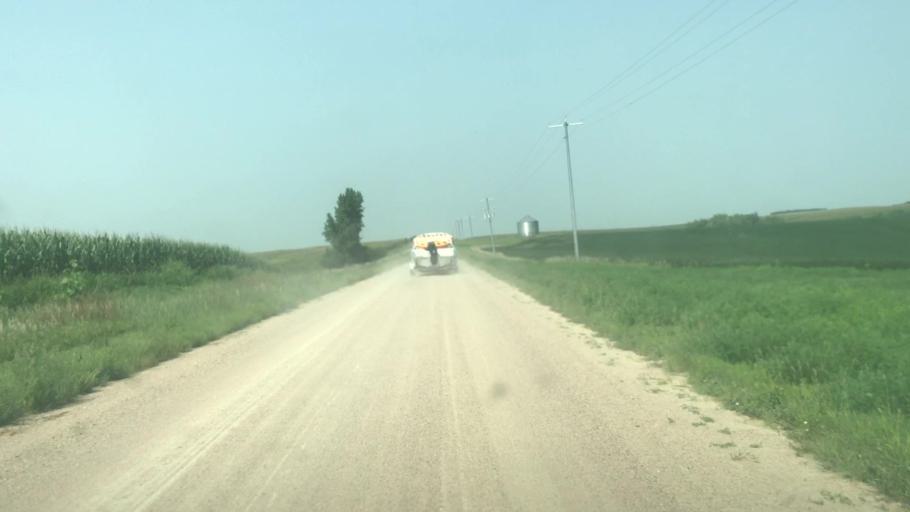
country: US
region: Nebraska
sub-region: Sherman County
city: Loup City
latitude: 41.2667
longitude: -98.9191
